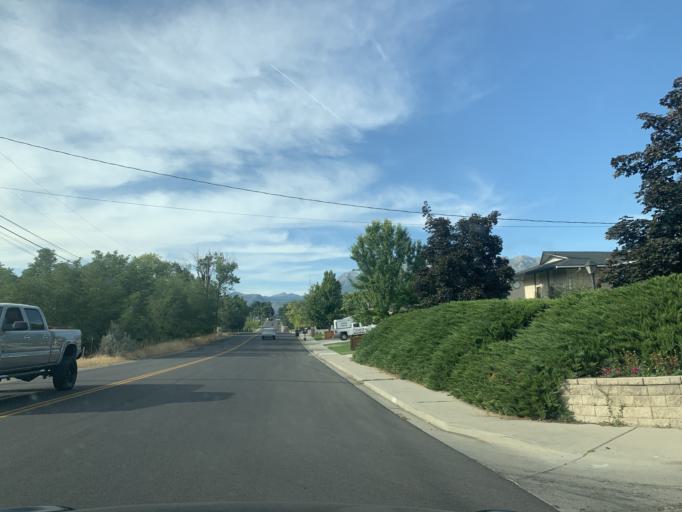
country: US
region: Utah
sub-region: Utah County
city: Orem
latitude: 40.2557
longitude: -111.6947
